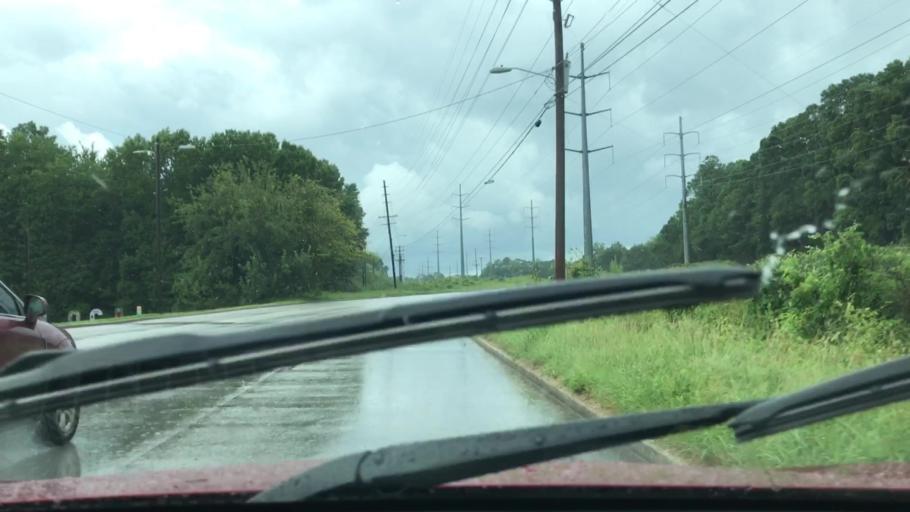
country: US
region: South Carolina
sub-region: Charleston County
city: North Charleston
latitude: 32.8468
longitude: -79.9920
